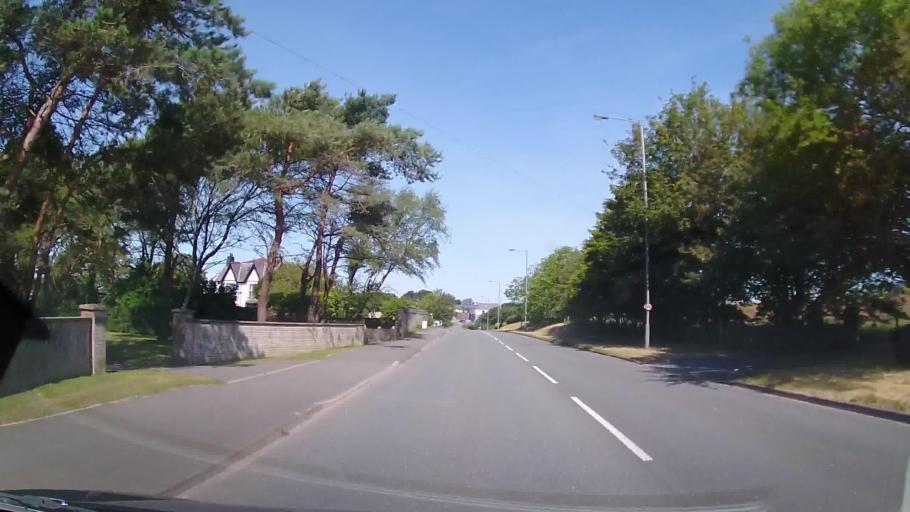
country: GB
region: Wales
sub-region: Gwynedd
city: Tywyn
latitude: 52.5815
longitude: -4.0772
